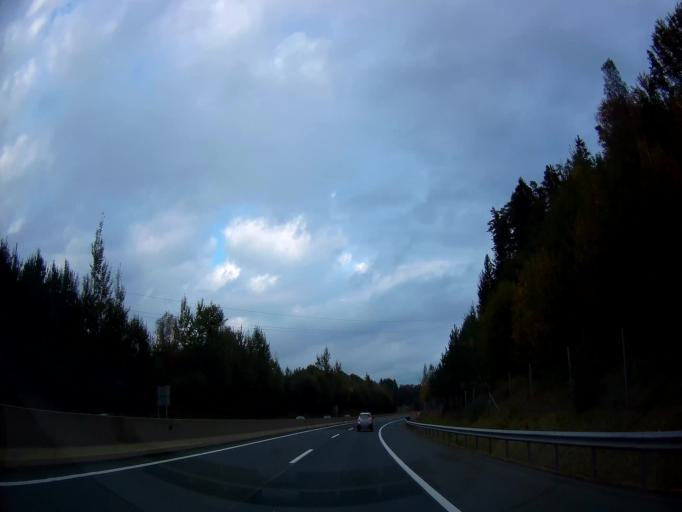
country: AT
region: Styria
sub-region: Politischer Bezirk Deutschlandsberg
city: Gundersdorf
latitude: 46.9698
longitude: 15.2493
